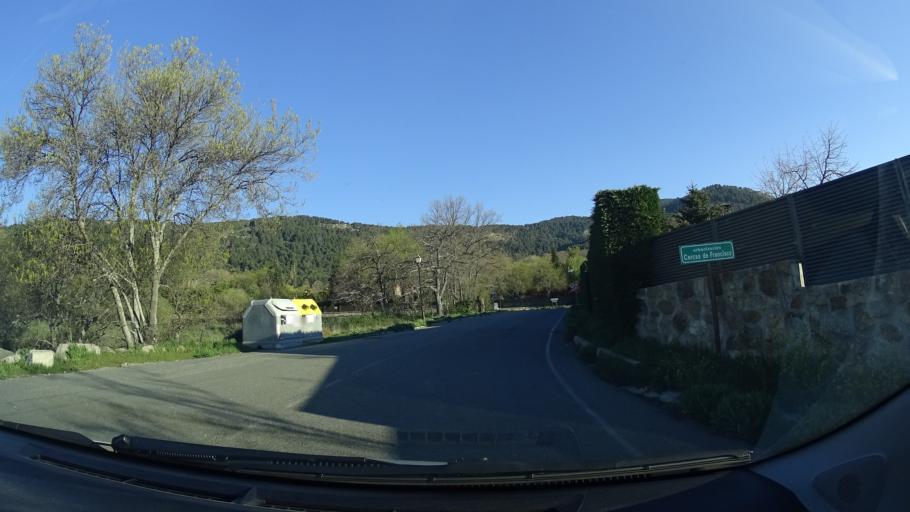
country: ES
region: Madrid
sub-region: Provincia de Madrid
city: Navacerrada
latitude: 40.7367
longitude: -4.0068
